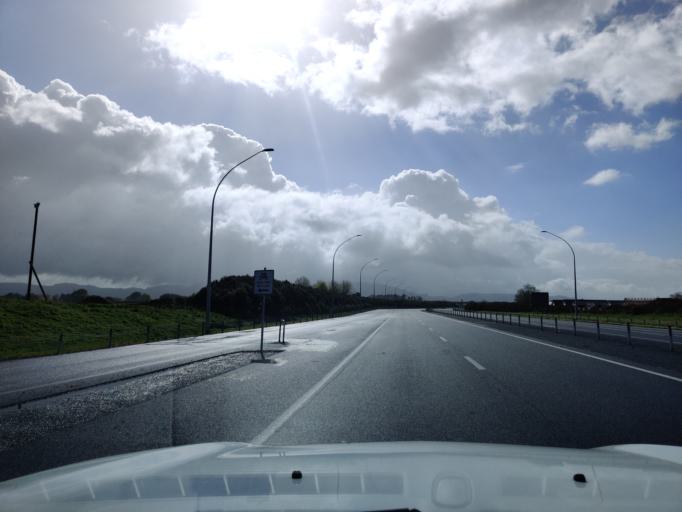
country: NZ
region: Waikato
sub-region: Waipa District
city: Cambridge
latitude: -37.8685
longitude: 175.4641
